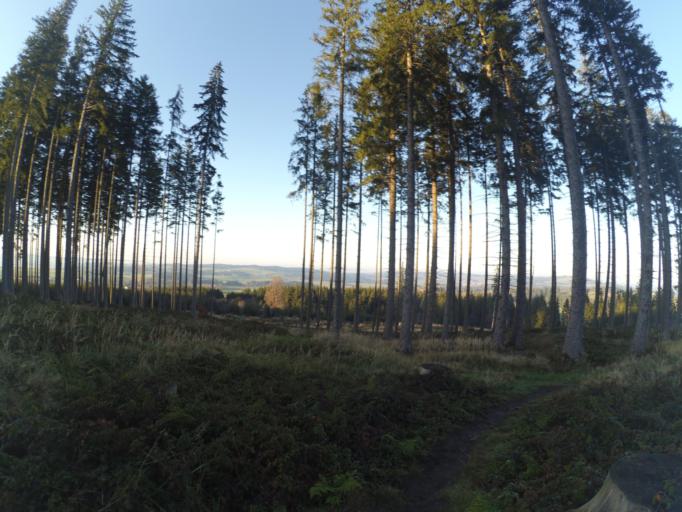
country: DE
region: Bavaria
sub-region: Upper Bavaria
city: Bernbeuren
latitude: 47.7371
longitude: 10.7364
